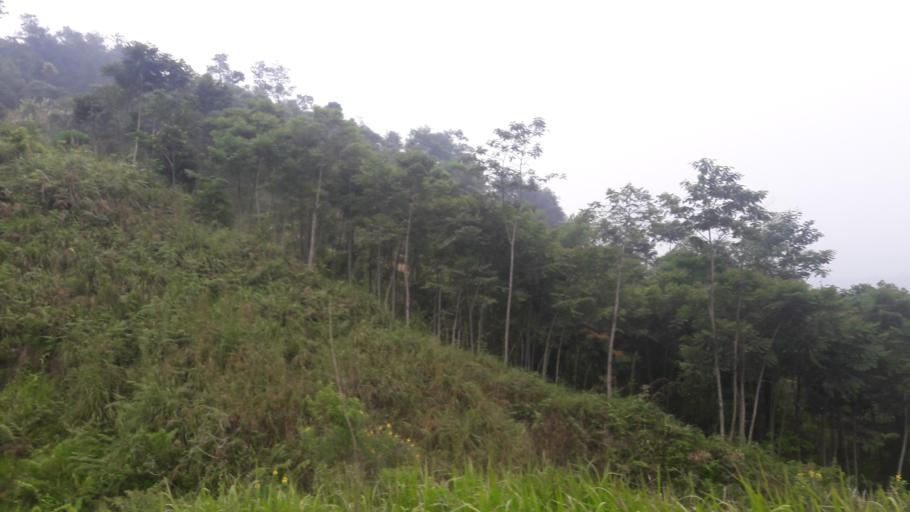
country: ID
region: West Java
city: Cipeundeuy
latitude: -6.6818
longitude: 106.5221
